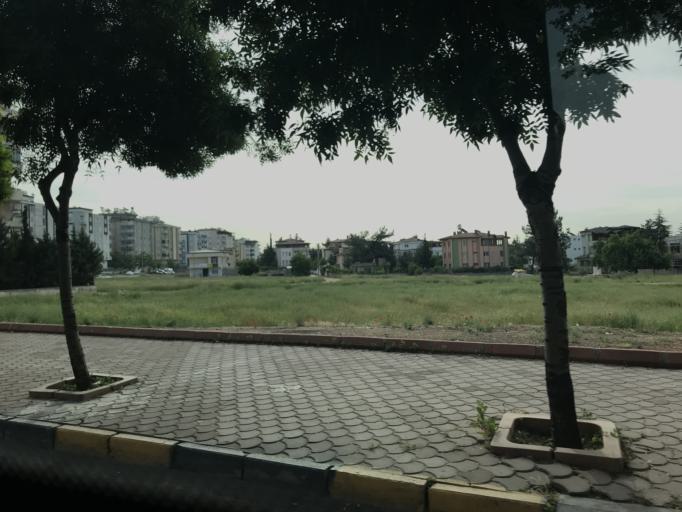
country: TR
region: Gaziantep
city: Sehitkamil
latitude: 37.0717
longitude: 37.3399
